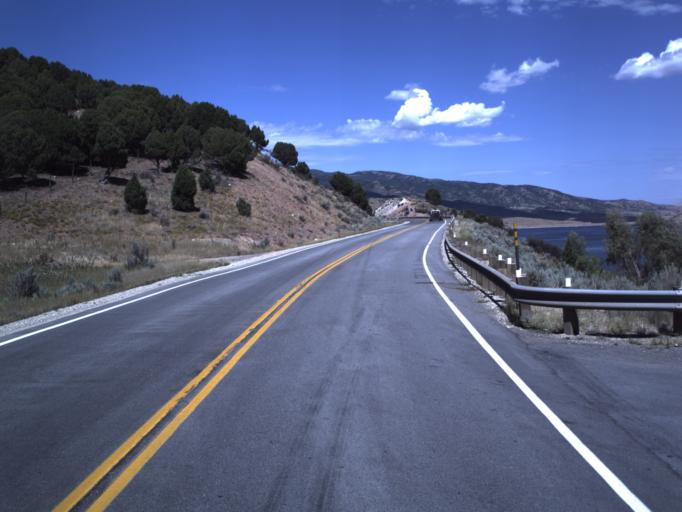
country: US
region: Utah
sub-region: Summit County
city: Oakley
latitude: 40.7637
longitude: -111.3977
